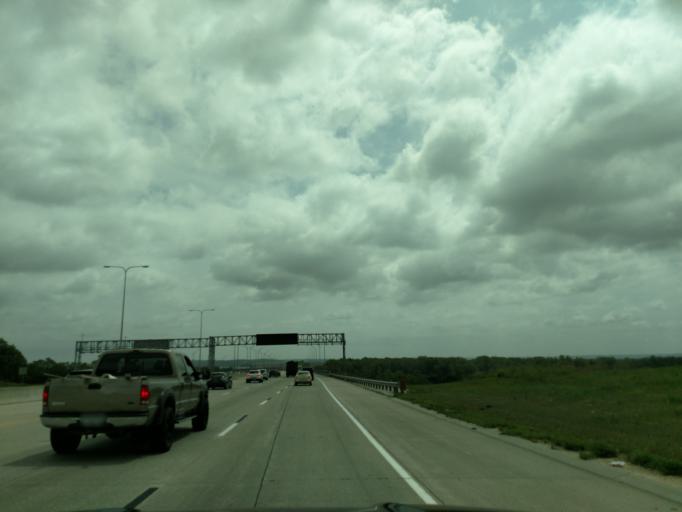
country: US
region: Nebraska
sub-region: Douglas County
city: Omaha
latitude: 41.2312
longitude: -95.9179
